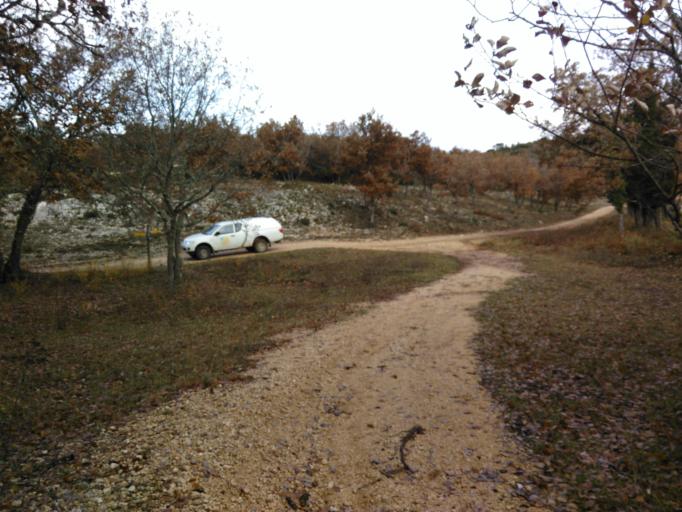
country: FR
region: Provence-Alpes-Cote d'Azur
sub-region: Departement du Vaucluse
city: Gordes
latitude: 43.9828
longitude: 5.2243
